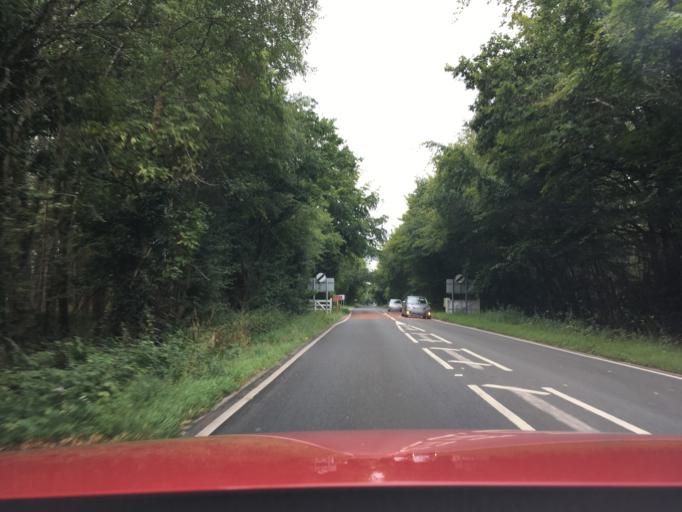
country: GB
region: England
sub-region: West Berkshire
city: Winterbourne
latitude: 51.4160
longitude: -1.3800
